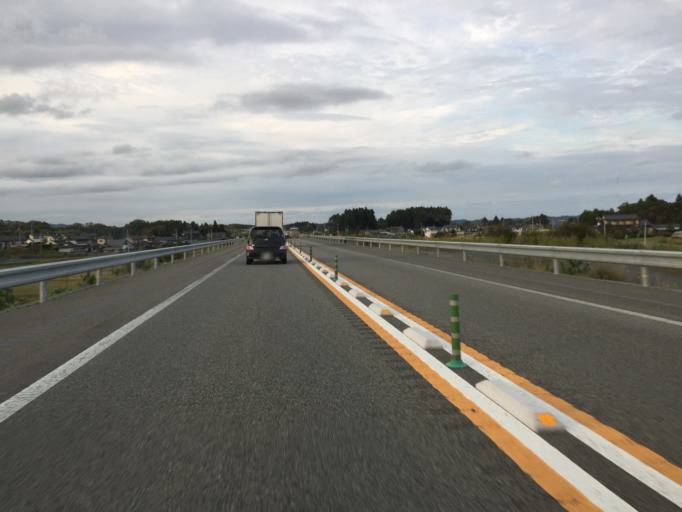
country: JP
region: Fukushima
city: Namie
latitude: 37.6092
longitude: 140.9260
